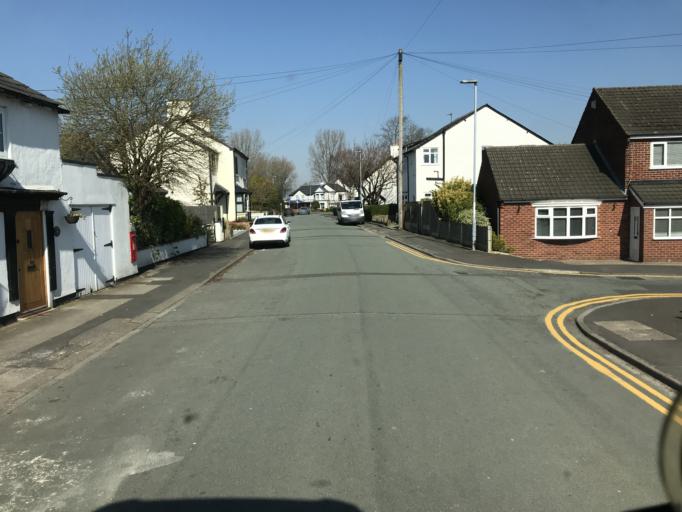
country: GB
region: England
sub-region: Trafford
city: Partington
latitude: 53.4149
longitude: -2.4562
